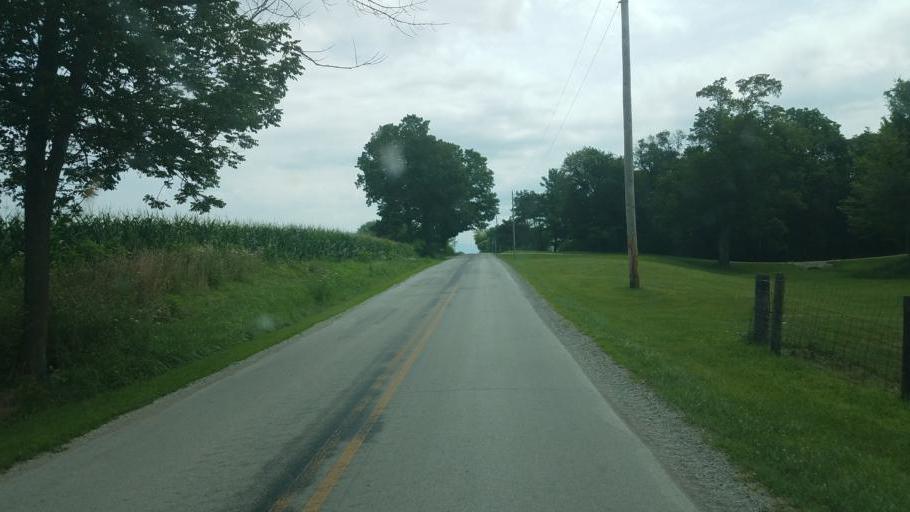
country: US
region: Ohio
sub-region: Wyandot County
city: Upper Sandusky
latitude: 40.8765
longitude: -83.2194
